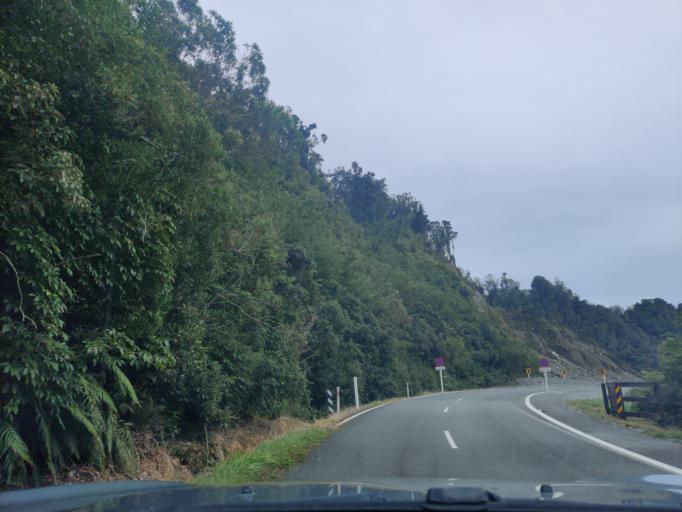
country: NZ
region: West Coast
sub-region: Westland District
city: Hokitika
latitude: -43.4069
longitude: 170.1777
